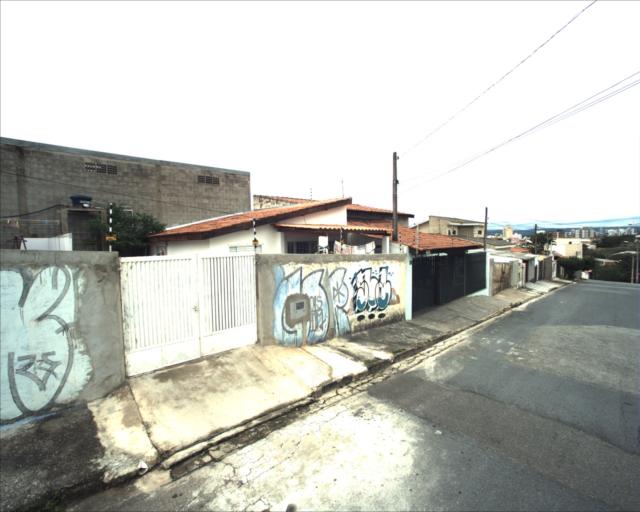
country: BR
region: Sao Paulo
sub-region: Sorocaba
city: Sorocaba
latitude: -23.4990
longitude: -47.4801
